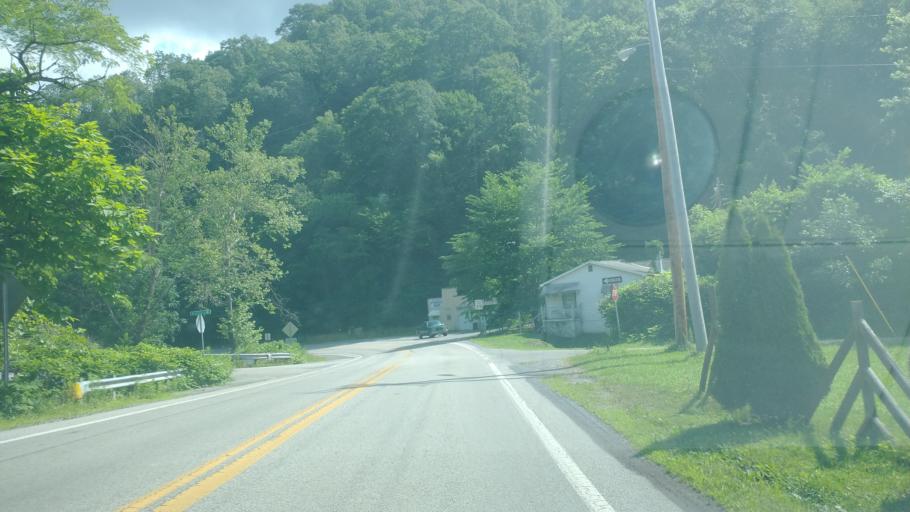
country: US
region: West Virginia
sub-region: McDowell County
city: Welch
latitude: 37.4287
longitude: -81.5060
